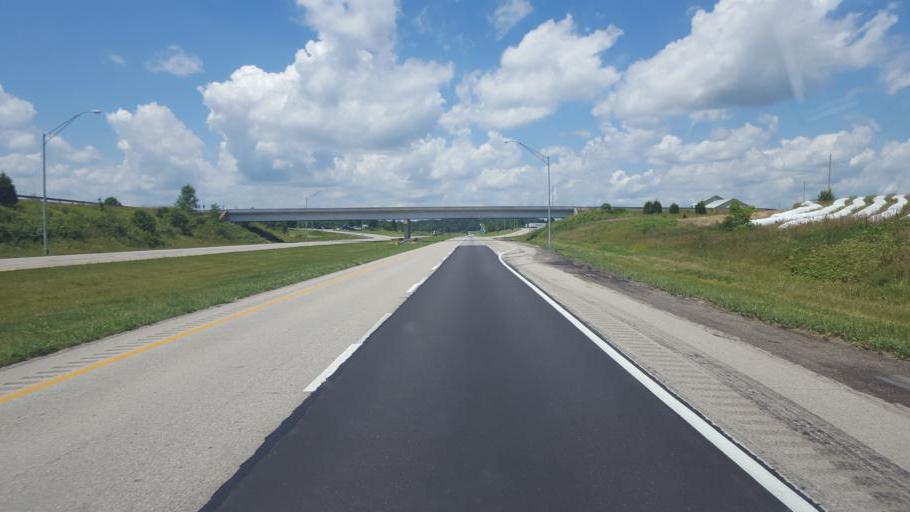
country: US
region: Ohio
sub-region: Gallia County
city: Gallipolis
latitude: 38.8818
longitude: -82.3274
